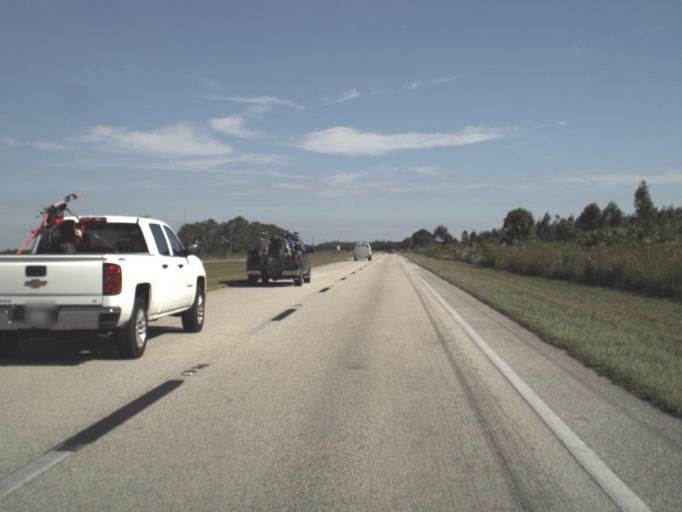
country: US
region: Florida
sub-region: Glades County
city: Moore Haven
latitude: 26.9062
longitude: -81.2633
